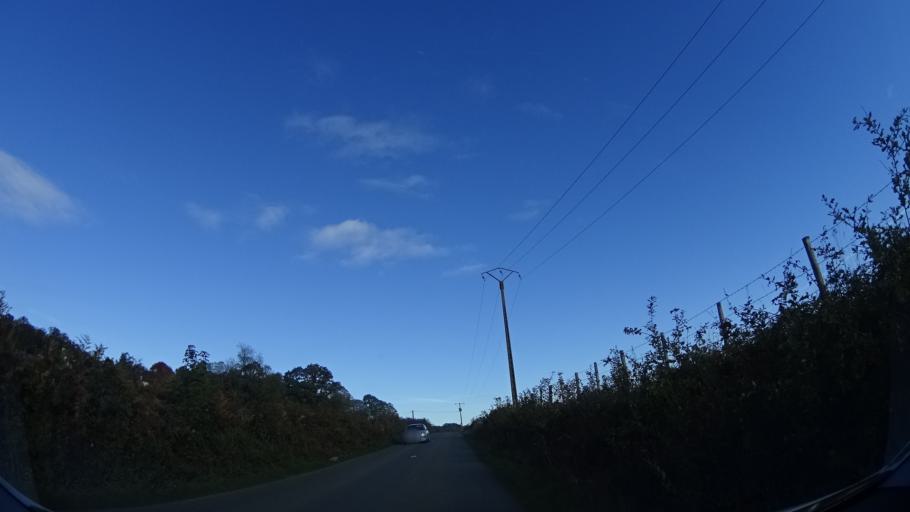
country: FR
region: Brittany
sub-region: Departement d'Ille-et-Vilaine
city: Geveze
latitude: 48.2096
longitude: -1.7911
